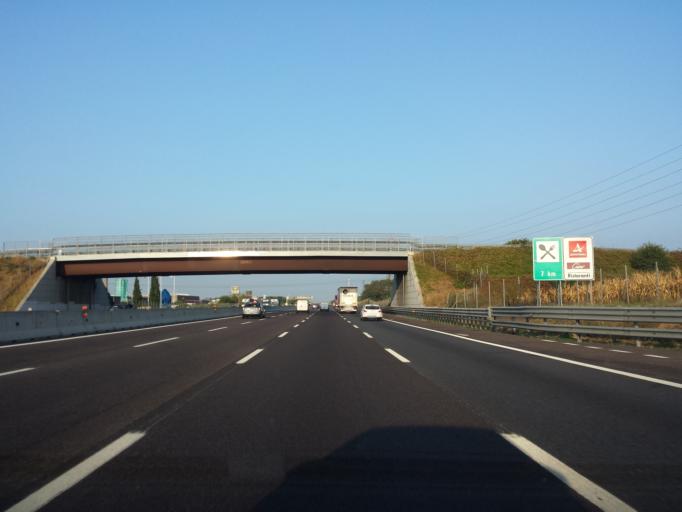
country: IT
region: Lombardy
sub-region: Citta metropolitana di Milano
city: Trezzano Rosa
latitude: 45.5916
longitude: 9.4805
